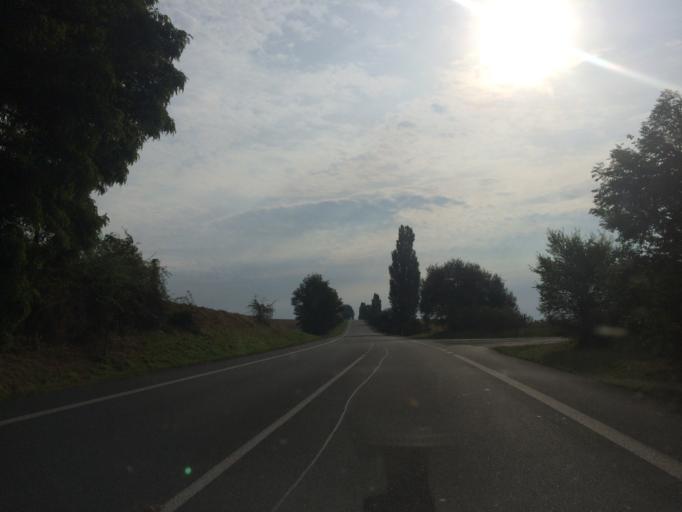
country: CZ
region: Central Bohemia
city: Poricany
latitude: 50.0526
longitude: 14.9146
